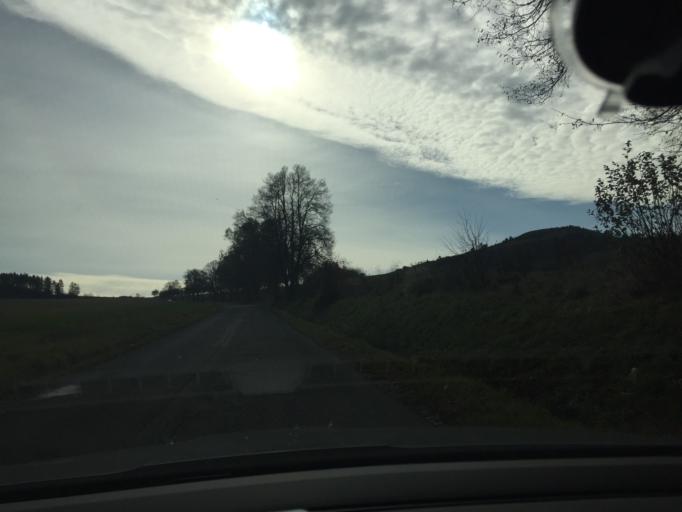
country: SK
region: Presovsky
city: Spisske Podhradie
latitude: 49.0048
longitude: 20.7765
